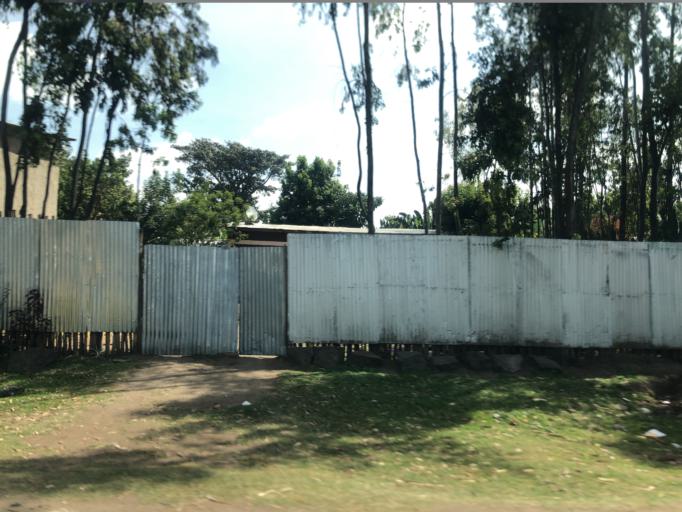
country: ET
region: Oromiya
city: Shashemene
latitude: 7.2270
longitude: 38.6300
